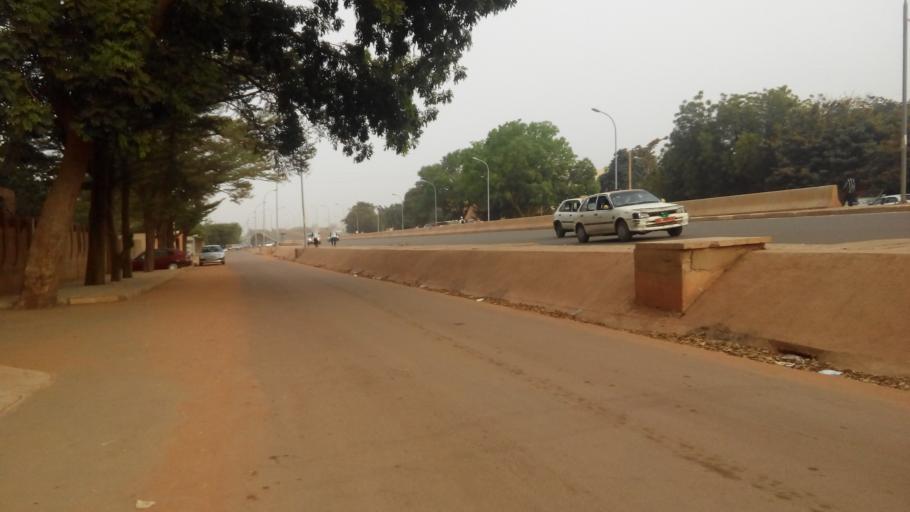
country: NE
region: Niamey
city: Niamey
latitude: 13.5343
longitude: 2.1045
